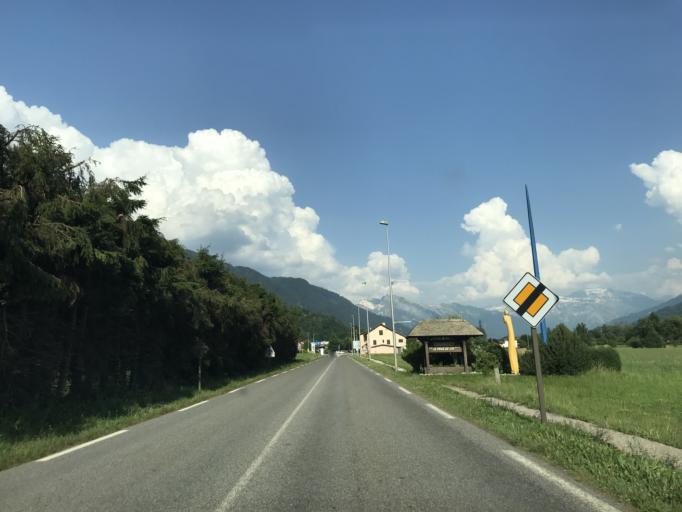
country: FR
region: Rhone-Alpes
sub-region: Departement de la Haute-Savoie
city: Taninges
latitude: 46.1084
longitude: 6.5787
